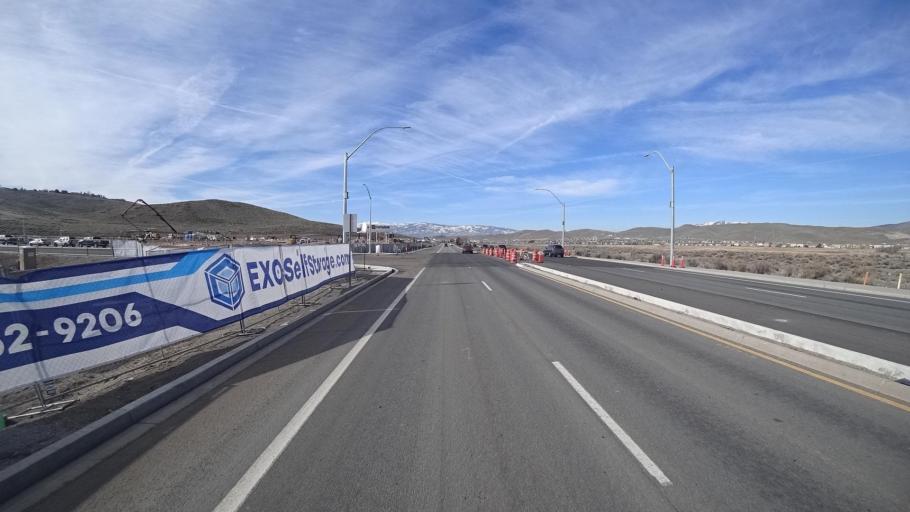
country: US
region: Nevada
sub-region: Washoe County
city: Spanish Springs
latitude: 39.6028
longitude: -119.7081
